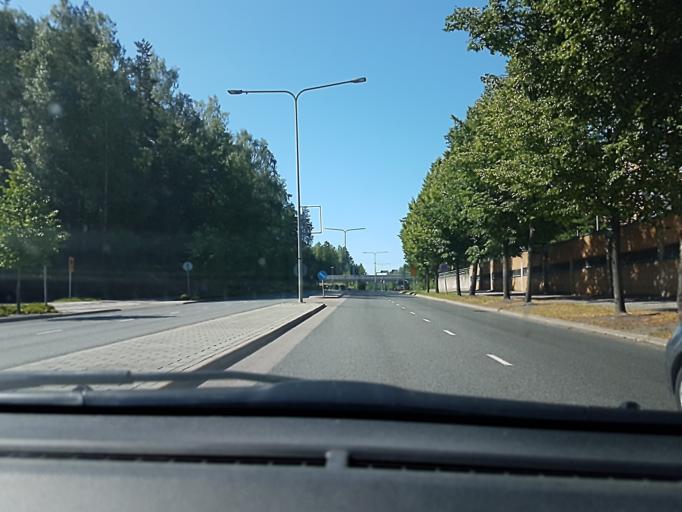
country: FI
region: Uusimaa
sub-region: Helsinki
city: Vantaa
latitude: 60.3219
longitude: 25.0537
